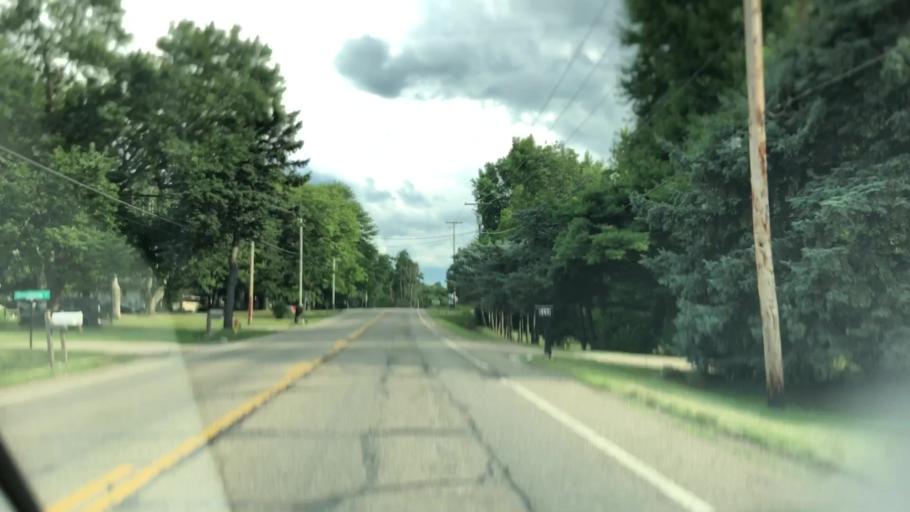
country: US
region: Ohio
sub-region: Summit County
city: Greensburg
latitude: 40.9226
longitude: -81.4634
